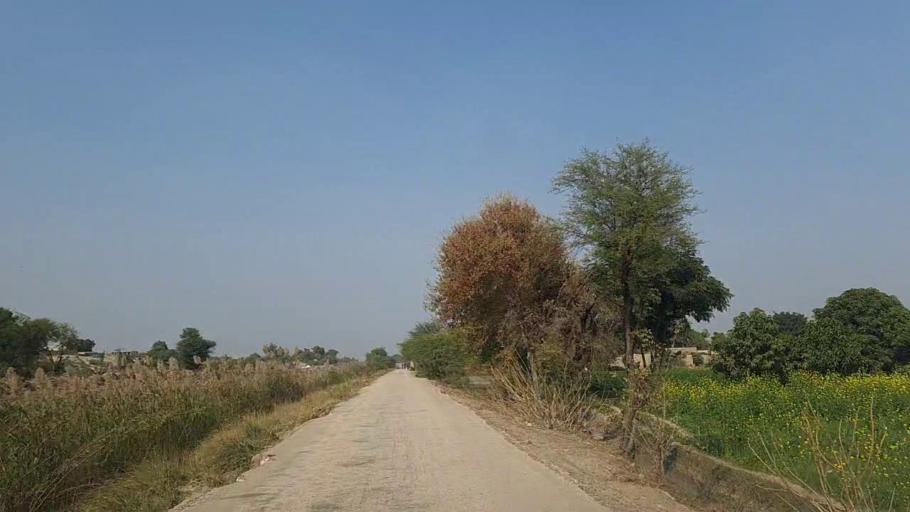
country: PK
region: Sindh
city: Daur
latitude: 26.4788
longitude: 68.4652
